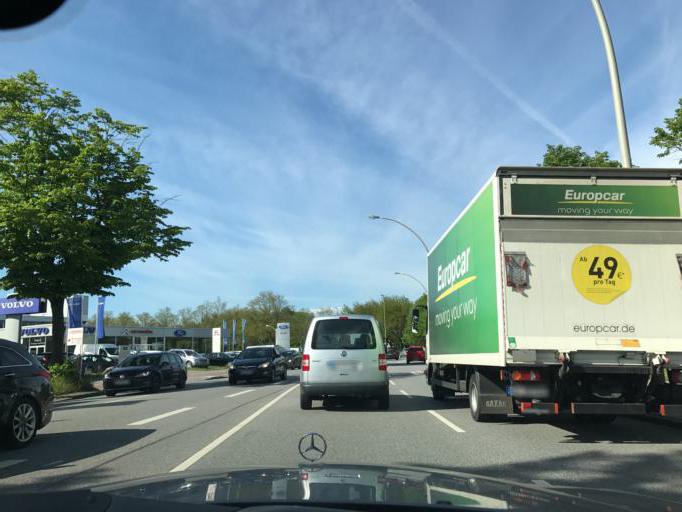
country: DE
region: Hamburg
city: Bergedorf
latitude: 53.4829
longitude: 10.2089
